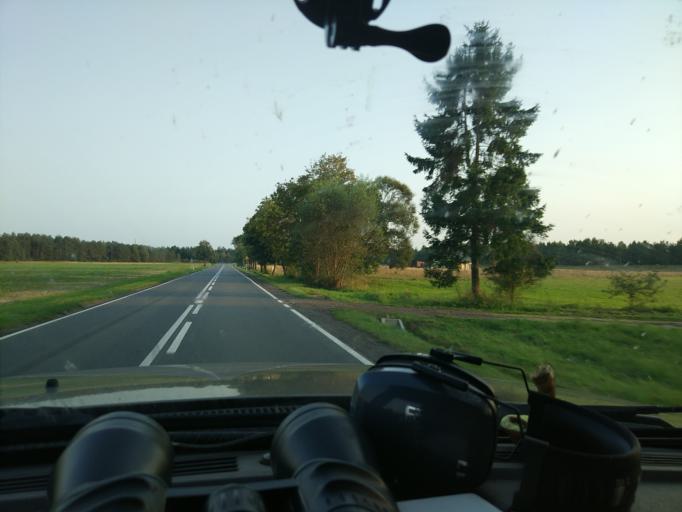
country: PL
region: Masovian Voivodeship
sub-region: Powiat przasnyski
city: Chorzele
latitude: 53.2779
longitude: 20.8990
